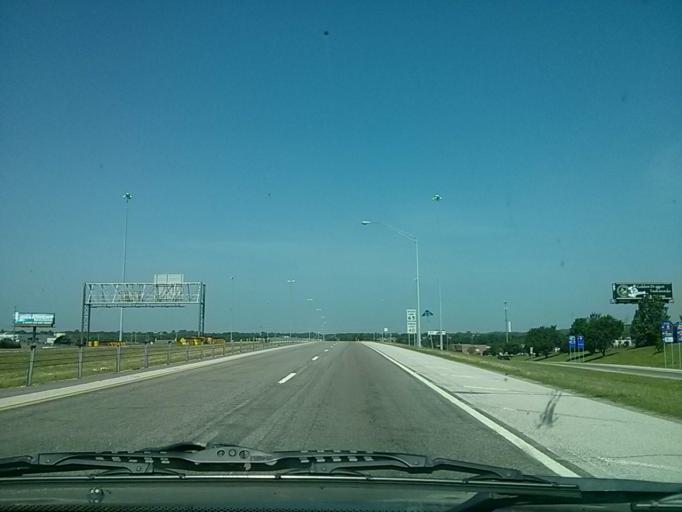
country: US
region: Oklahoma
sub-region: Tulsa County
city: Bixby
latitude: 36.0255
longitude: -95.8815
